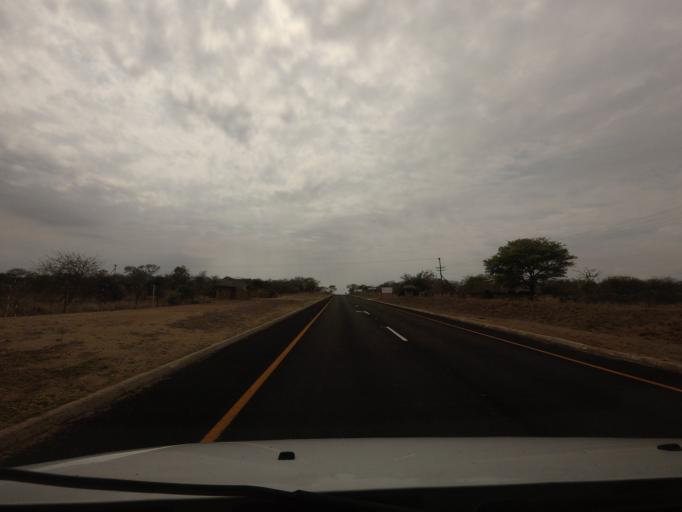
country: ZA
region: Limpopo
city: Thulamahashi
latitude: -24.5561
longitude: 31.2225
